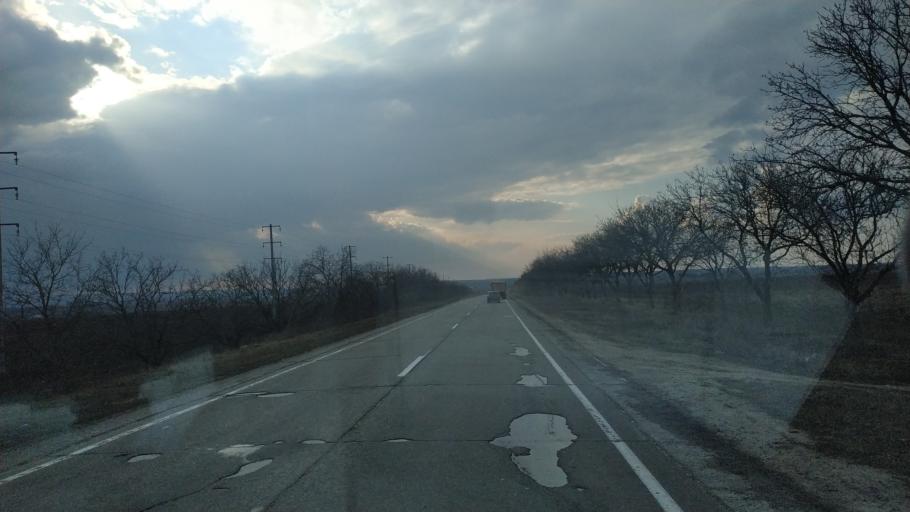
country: MD
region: Anenii Noi
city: Varnita
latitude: 46.9215
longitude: 29.3702
